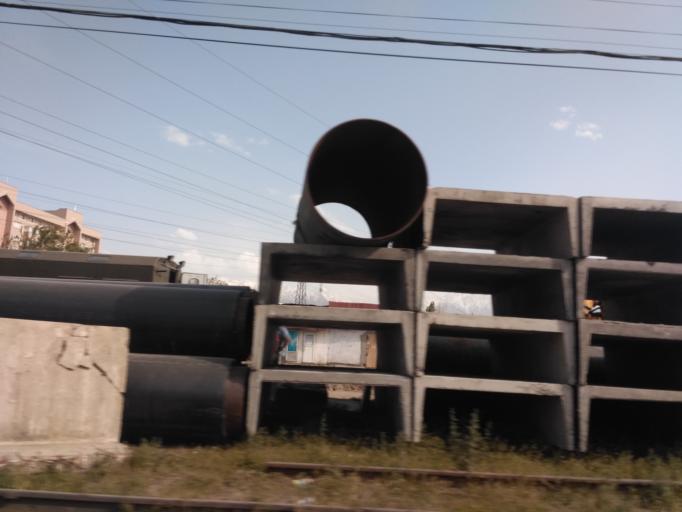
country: KZ
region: Almaty Qalasy
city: Almaty
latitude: 43.2445
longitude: 76.8508
